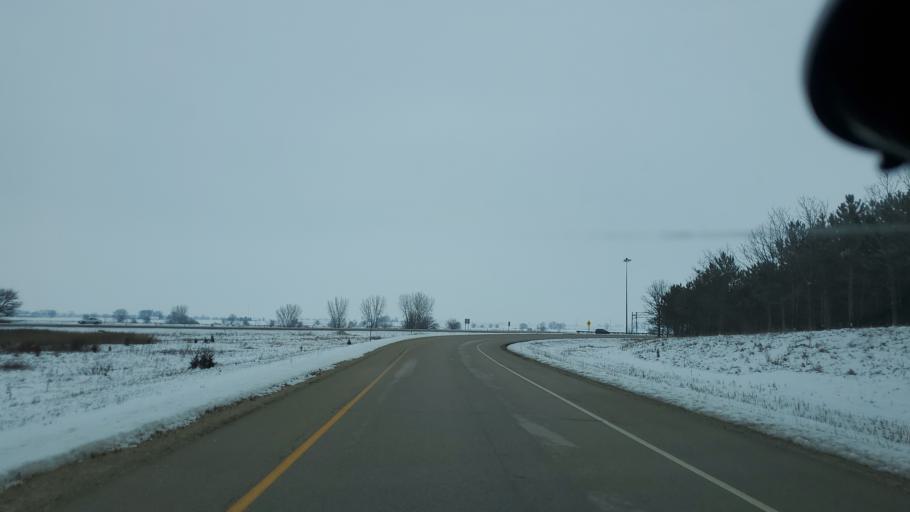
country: US
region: Illinois
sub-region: Ogle County
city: Rochelle
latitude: 41.9037
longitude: -89.0167
